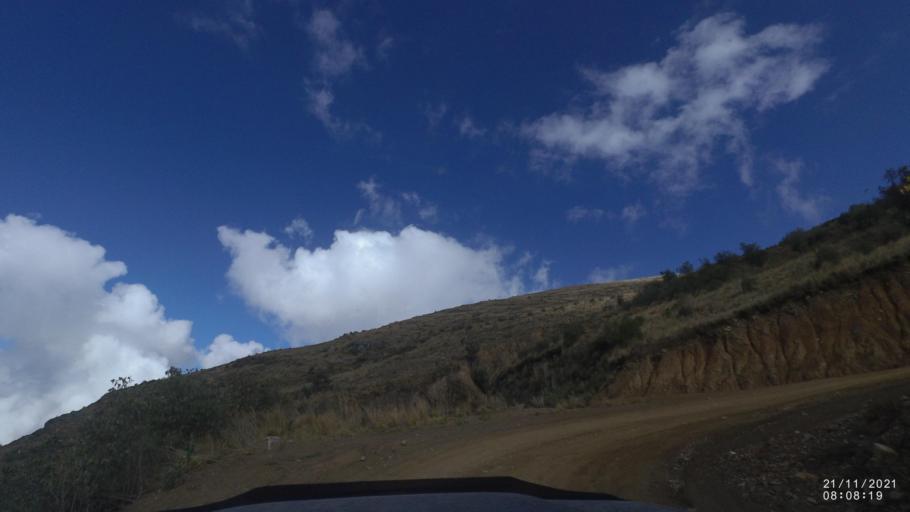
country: BO
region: Cochabamba
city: Cochabamba
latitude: -17.2860
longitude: -66.2123
